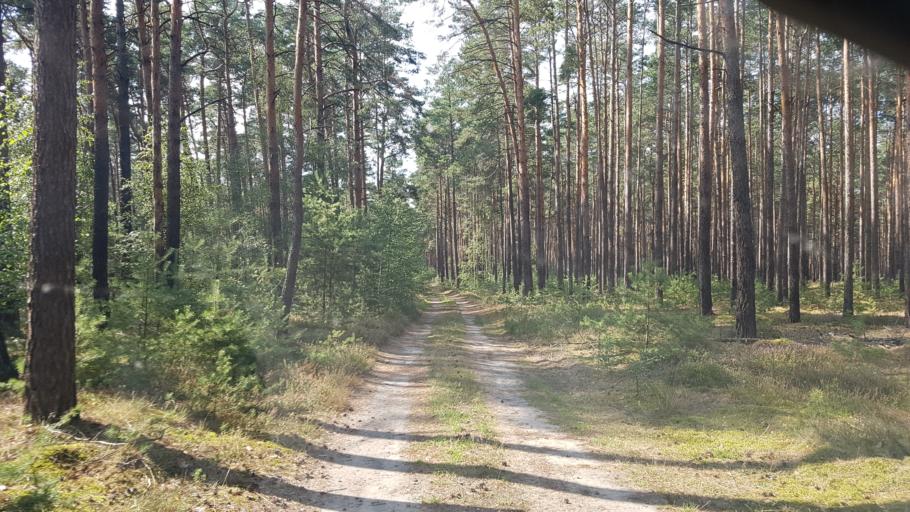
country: DE
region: Brandenburg
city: Sonnewalde
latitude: 51.6442
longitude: 13.6541
